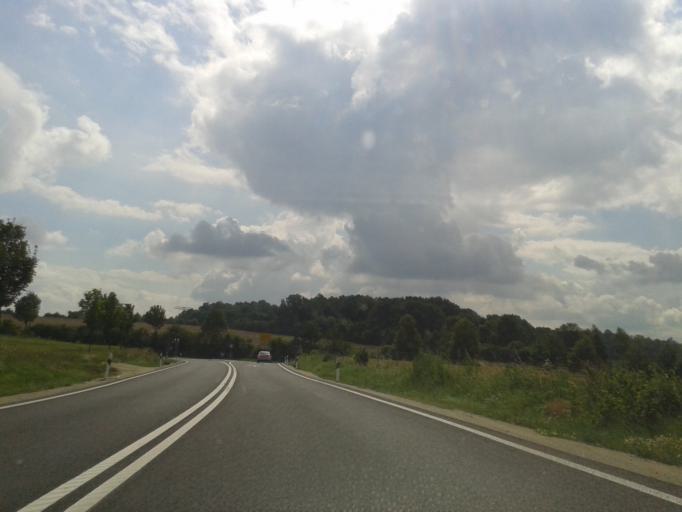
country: DE
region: Saxony
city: Goda
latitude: 51.1915
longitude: 14.3583
